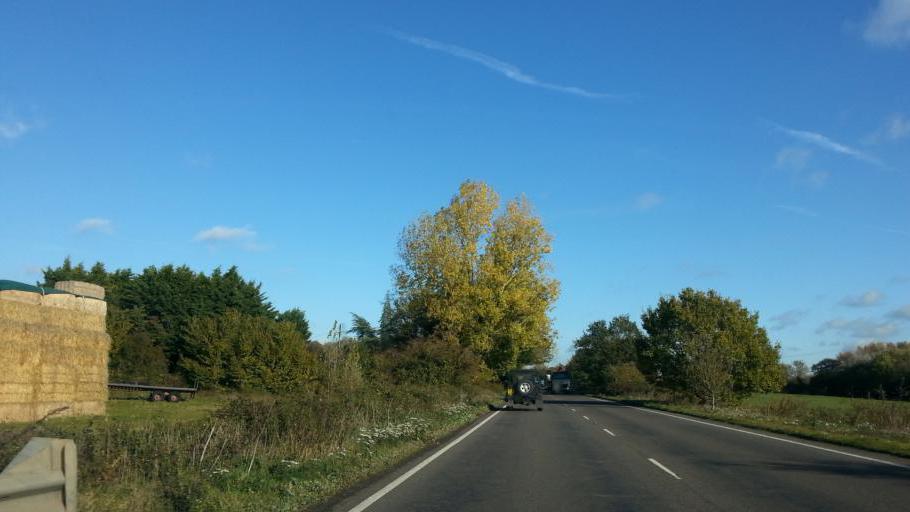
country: GB
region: England
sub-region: Suffolk
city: Bungay
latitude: 52.4314
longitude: 1.3718
